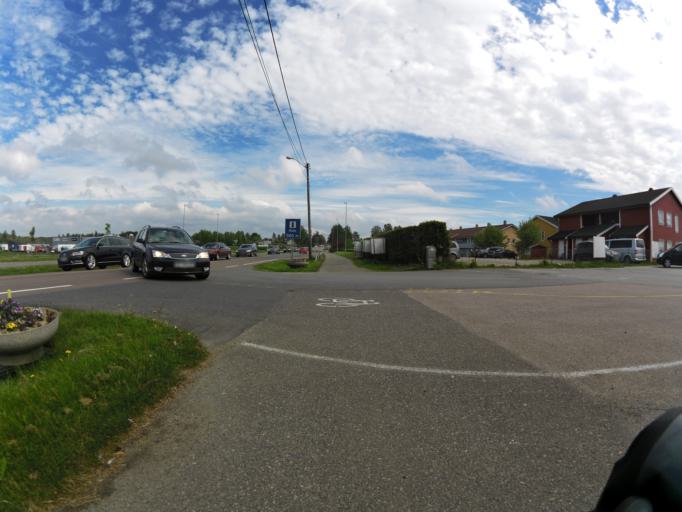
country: NO
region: Ostfold
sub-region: Rade
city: Karlshus
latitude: 59.3544
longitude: 10.8512
